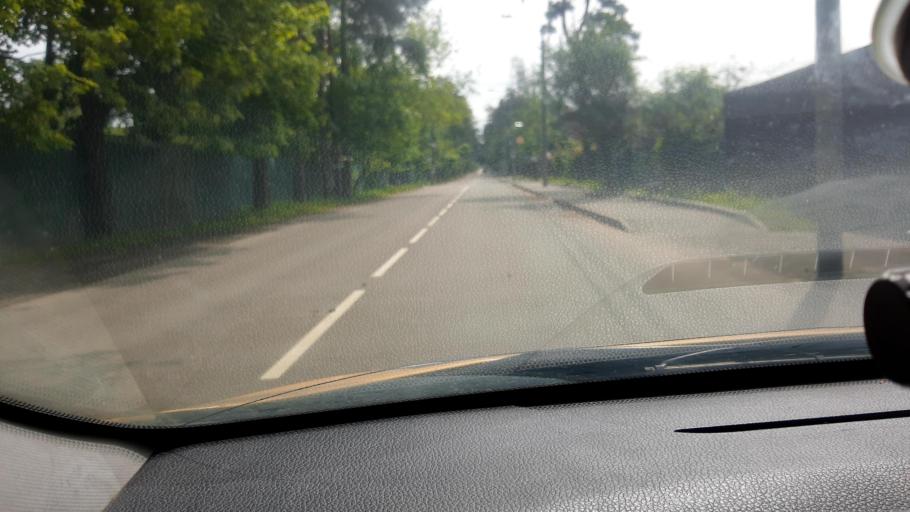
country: RU
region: Moscow
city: Mikhalkovo
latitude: 55.6740
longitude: 37.4120
